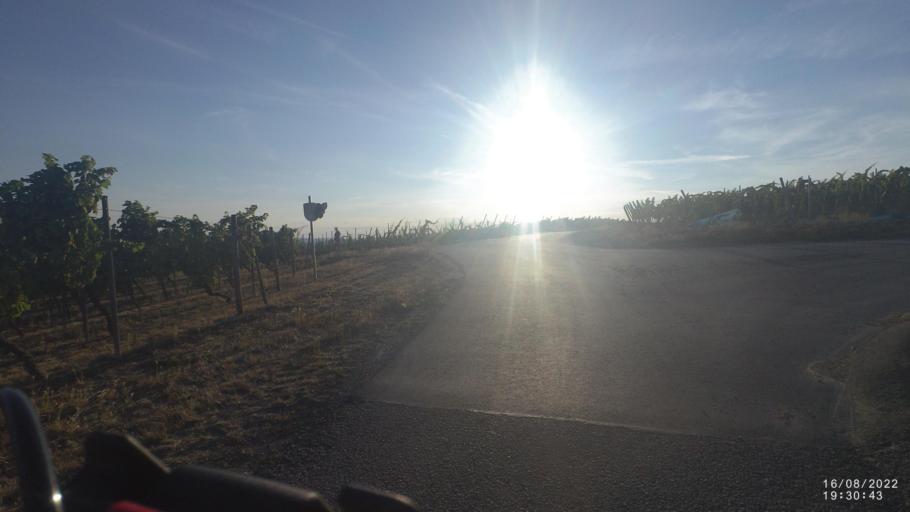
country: DE
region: Rheinland-Pfalz
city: Ensheim
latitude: 49.8023
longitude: 8.1193
